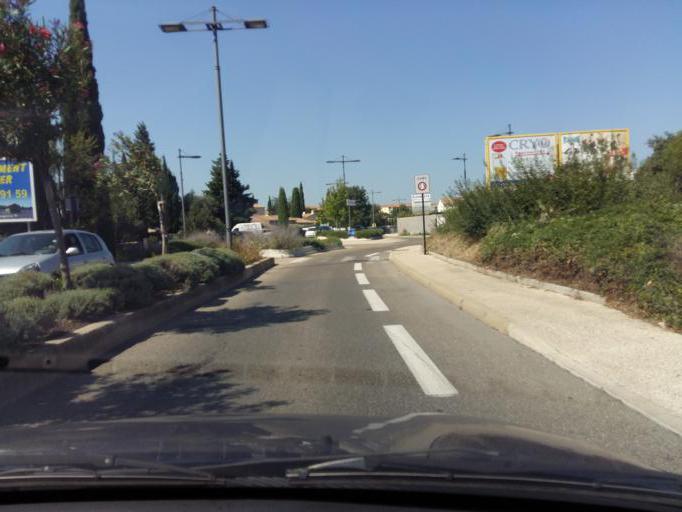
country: FR
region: Languedoc-Roussillon
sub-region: Departement du Gard
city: Les Angles
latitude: 43.9586
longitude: 4.7574
